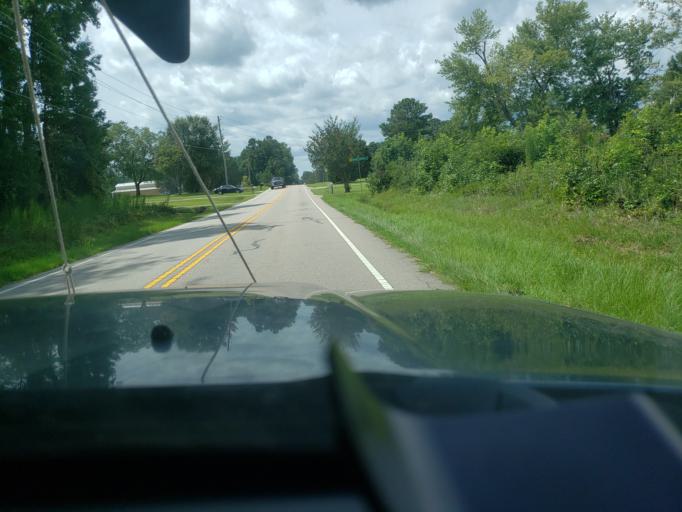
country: US
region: North Carolina
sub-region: Wake County
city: Rolesville
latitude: 35.8780
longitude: -78.4522
